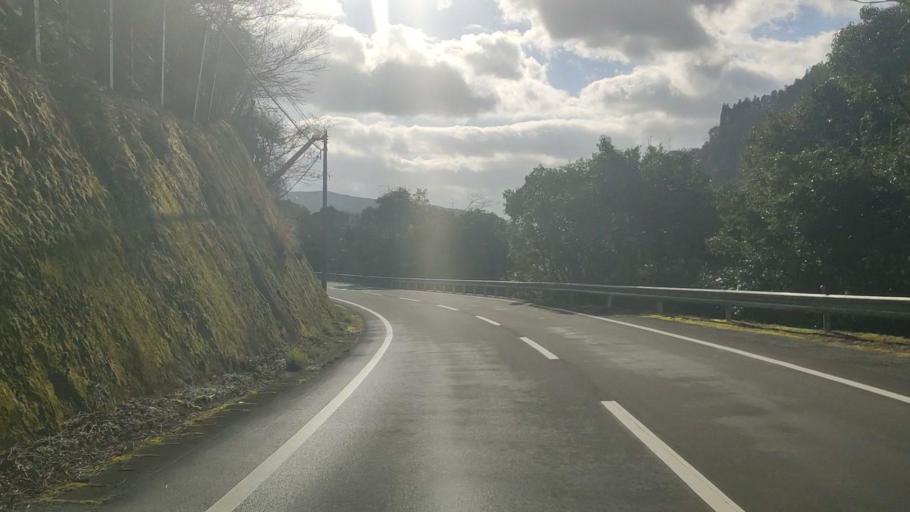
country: JP
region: Kumamoto
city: Hitoyoshi
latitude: 32.3199
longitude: 130.8418
